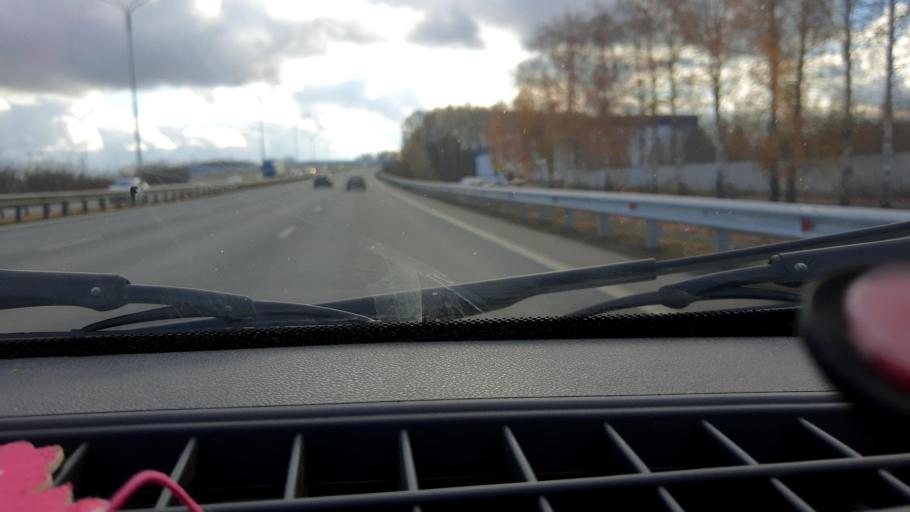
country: RU
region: Bashkortostan
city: Ufa
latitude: 54.5823
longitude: 55.9124
